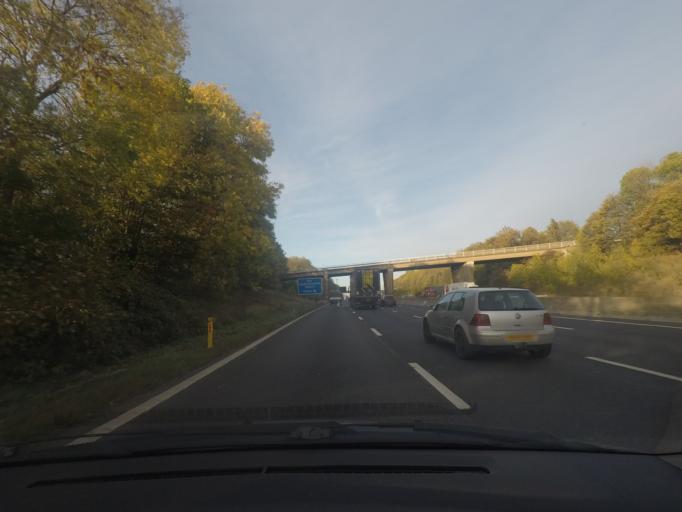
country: GB
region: England
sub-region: City and Borough of Wakefield
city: Ossett
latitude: 53.7021
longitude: -1.5552
